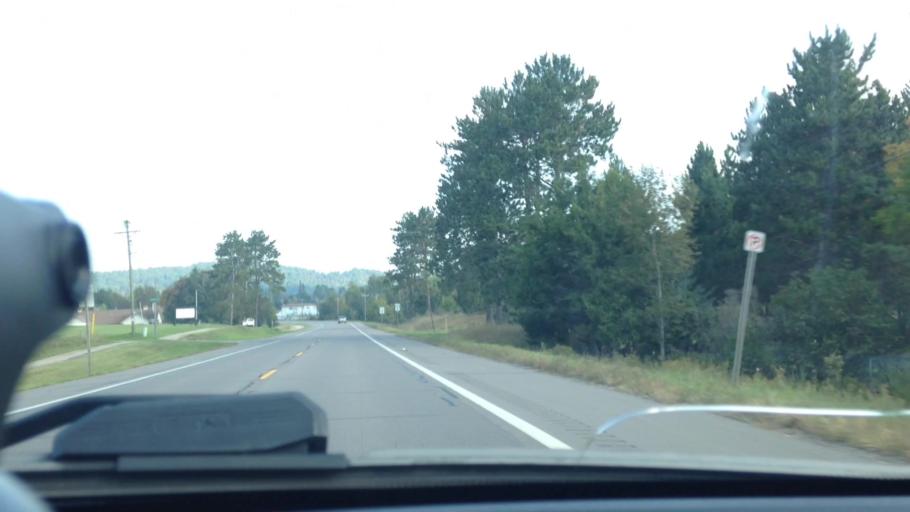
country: US
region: Michigan
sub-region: Dickinson County
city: Norway
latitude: 45.7757
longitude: -87.9090
